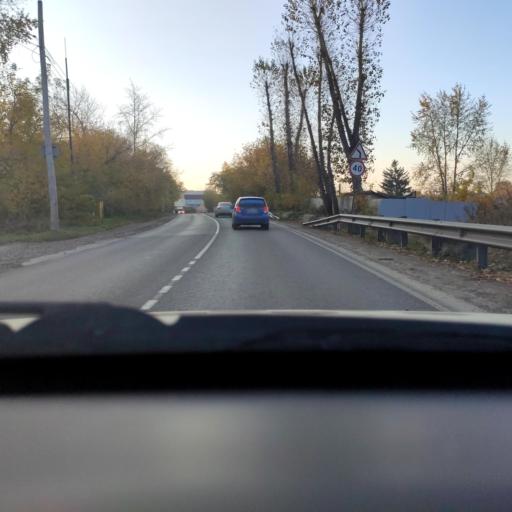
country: RU
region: Perm
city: Kondratovo
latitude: 57.9654
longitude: 56.1278
